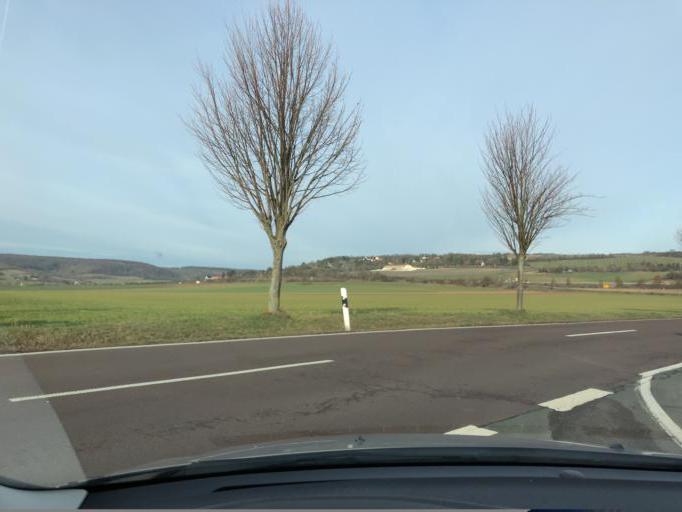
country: DE
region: Saxony-Anhalt
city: Freyburg
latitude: 51.1997
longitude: 11.7984
